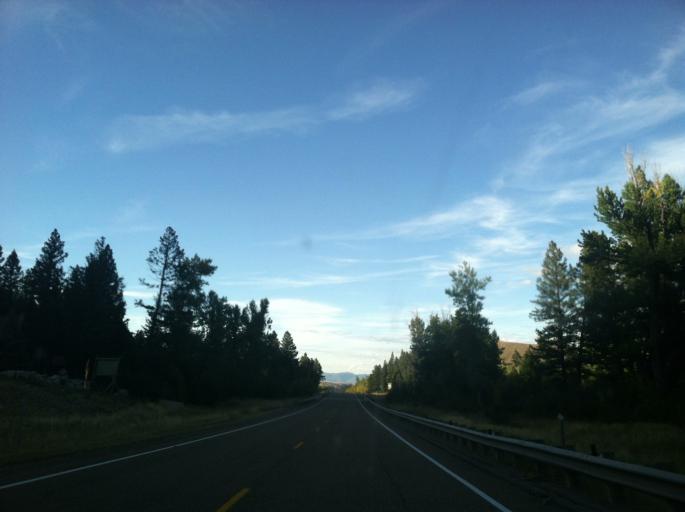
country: US
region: Montana
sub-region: Granite County
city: Philipsburg
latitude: 46.4684
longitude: -113.2348
